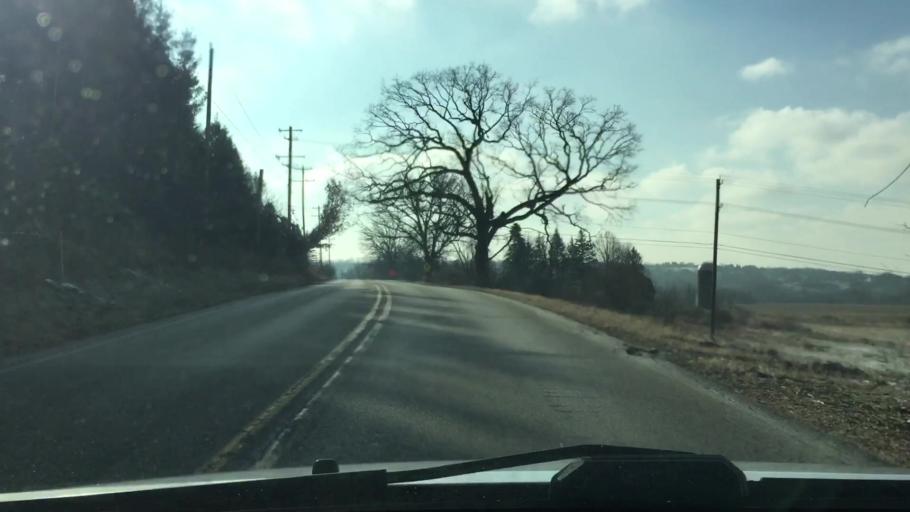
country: US
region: Wisconsin
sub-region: Waukesha County
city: Waukesha
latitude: 43.0030
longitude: -88.2903
